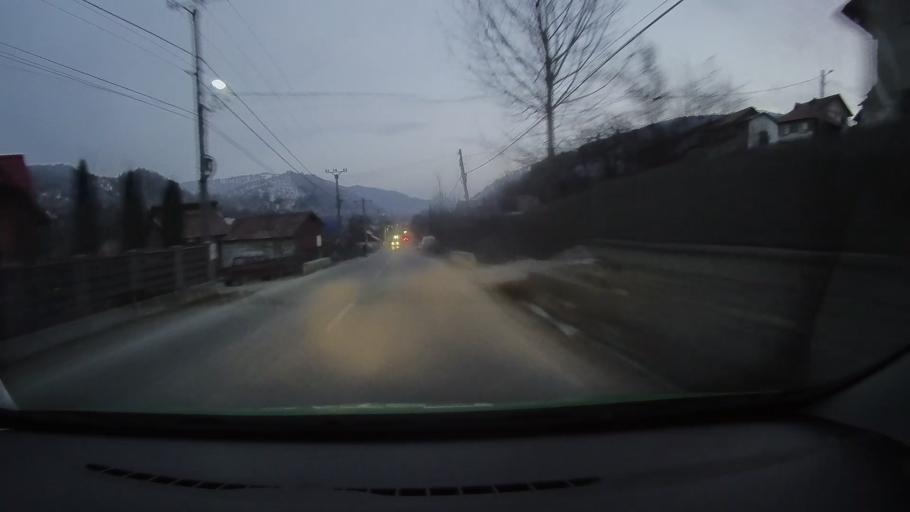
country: RO
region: Prahova
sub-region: Comuna Valea Doftanei
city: Tesila
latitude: 45.2957
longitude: 25.7205
